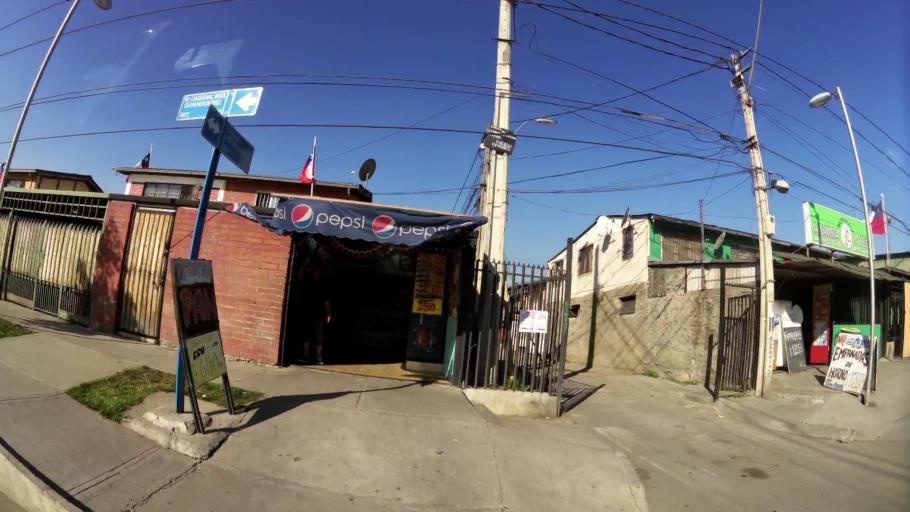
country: CL
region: Santiago Metropolitan
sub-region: Provincia de Santiago
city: La Pintana
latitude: -33.5503
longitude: -70.6180
